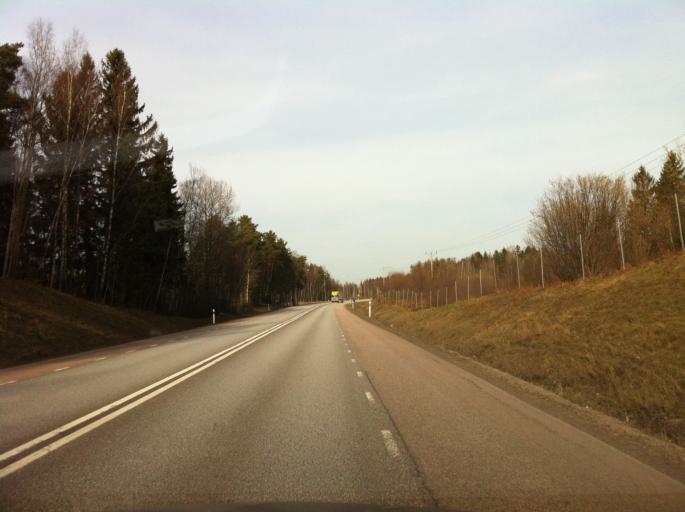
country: SE
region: Vaestra Goetaland
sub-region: Mariestads Kommun
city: Mariestad
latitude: 58.7113
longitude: 13.8764
